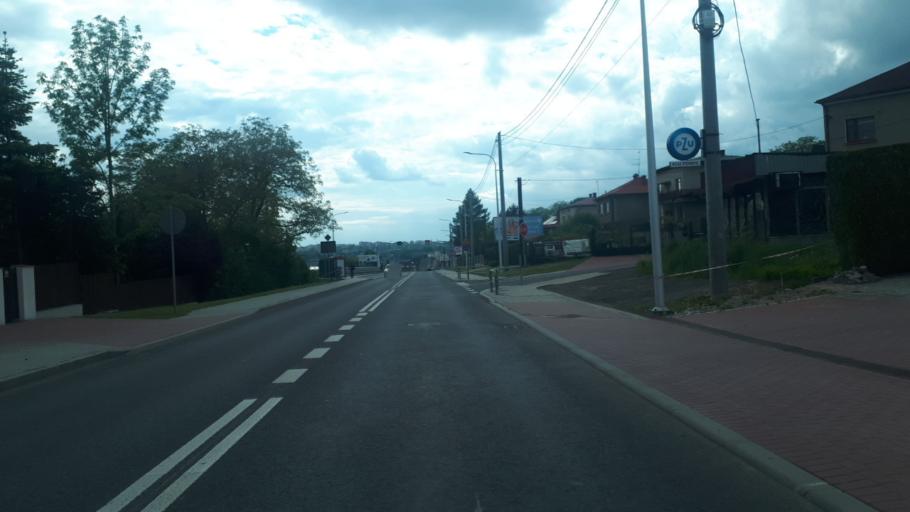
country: PL
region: Silesian Voivodeship
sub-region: Bielsko-Biala
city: Bielsko-Biala
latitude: 49.8209
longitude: 19.0718
